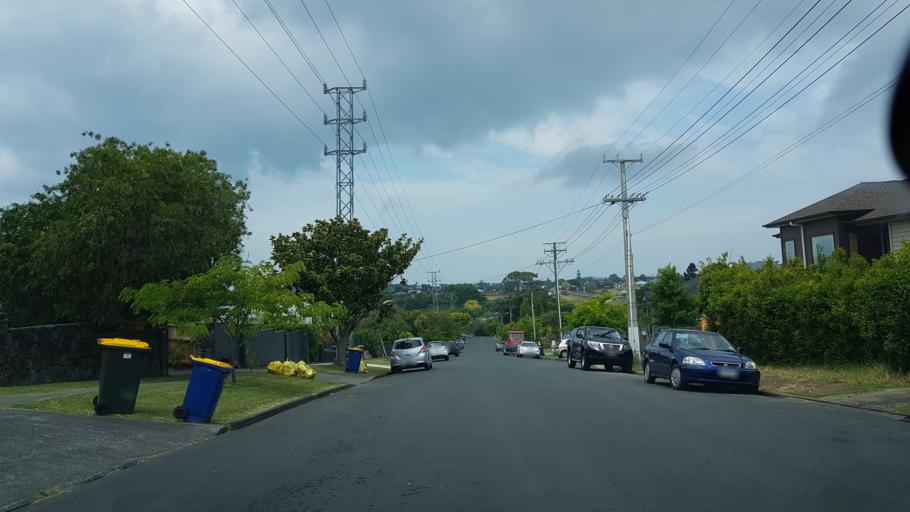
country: NZ
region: Auckland
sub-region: Auckland
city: North Shore
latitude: -36.8020
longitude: 174.7771
